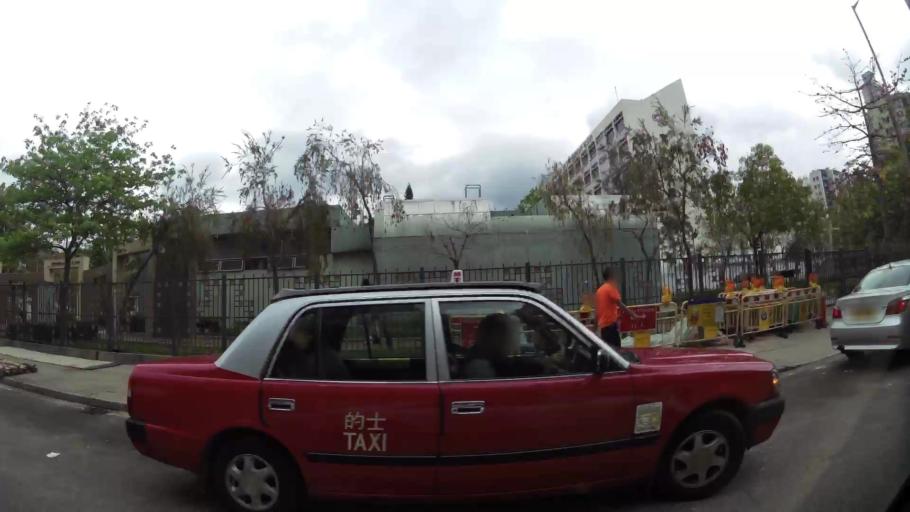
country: HK
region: Sham Shui Po
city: Sham Shui Po
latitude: 22.3298
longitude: 114.1559
